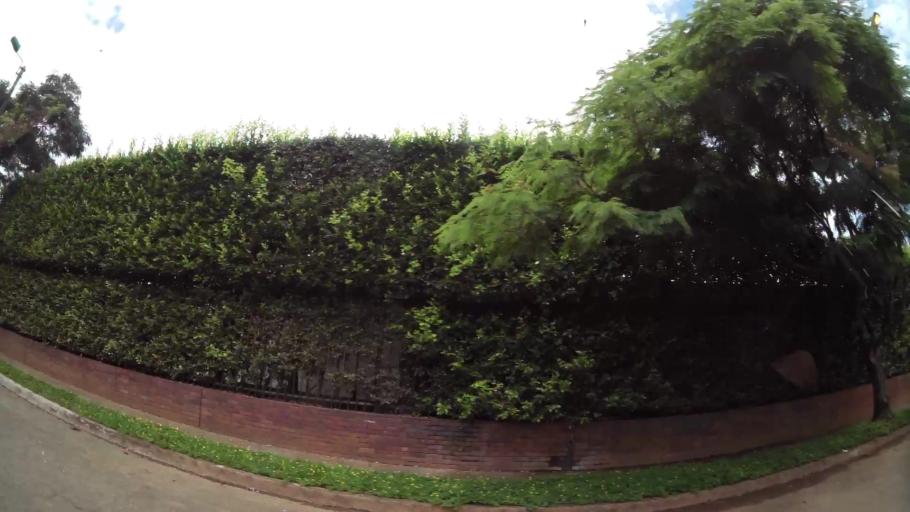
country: CO
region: Valle del Cauca
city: Cali
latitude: 3.3862
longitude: -76.5338
